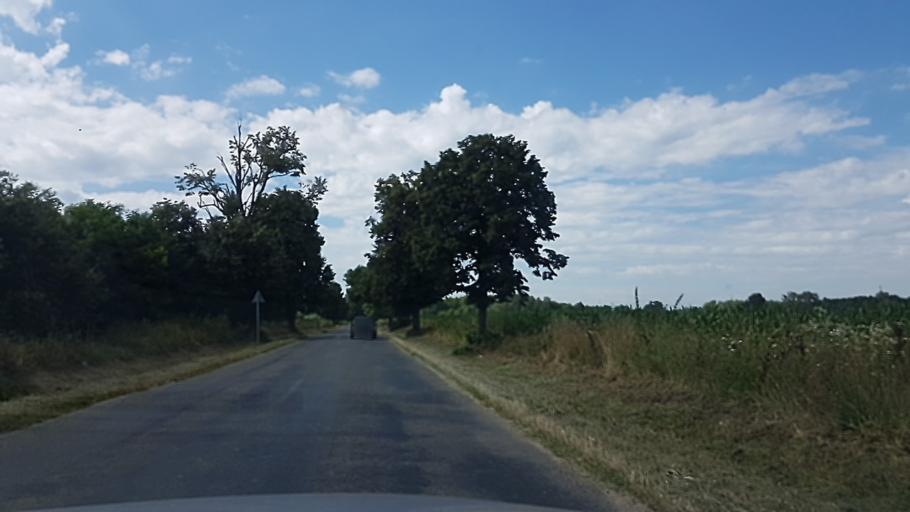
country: HU
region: Somogy
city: Barcs
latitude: 45.9558
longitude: 17.5991
